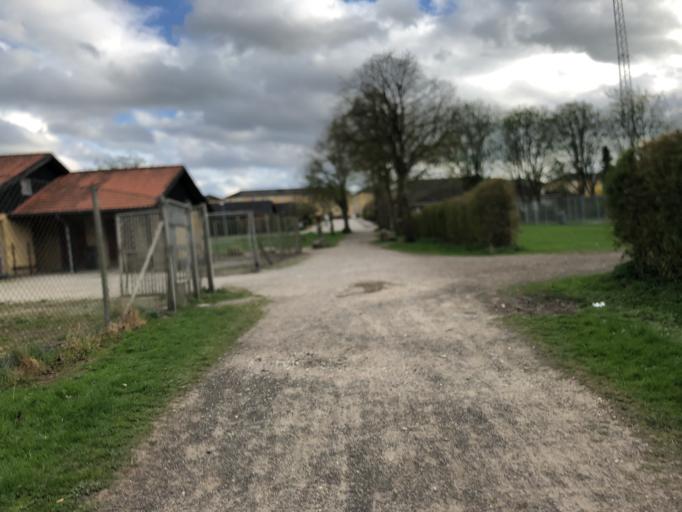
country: DK
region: Zealand
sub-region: Ringsted Kommune
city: Ringsted
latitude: 55.4462
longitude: 11.8061
